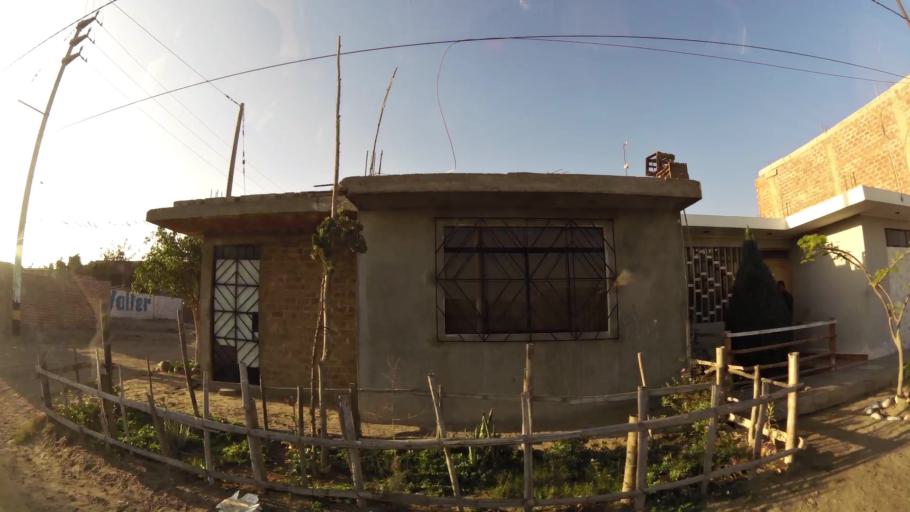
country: PE
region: Ica
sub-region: Provincia de Pisco
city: Villa Tupac Amaru
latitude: -13.7184
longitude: -76.1509
